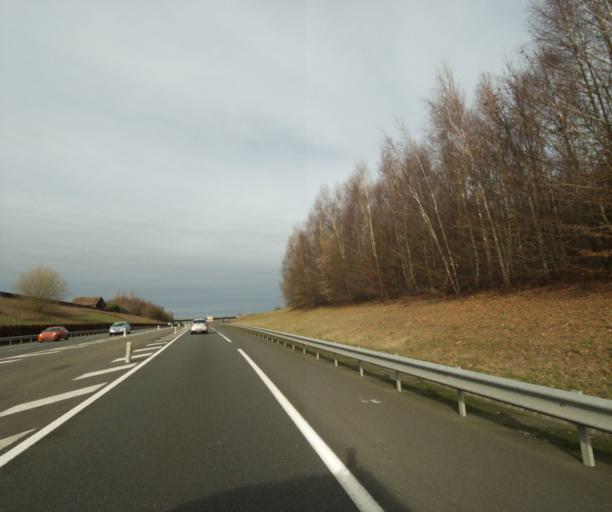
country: FR
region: Pays de la Loire
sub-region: Departement de la Sarthe
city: Sarge-les-le-Mans
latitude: 48.0139
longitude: 0.2420
